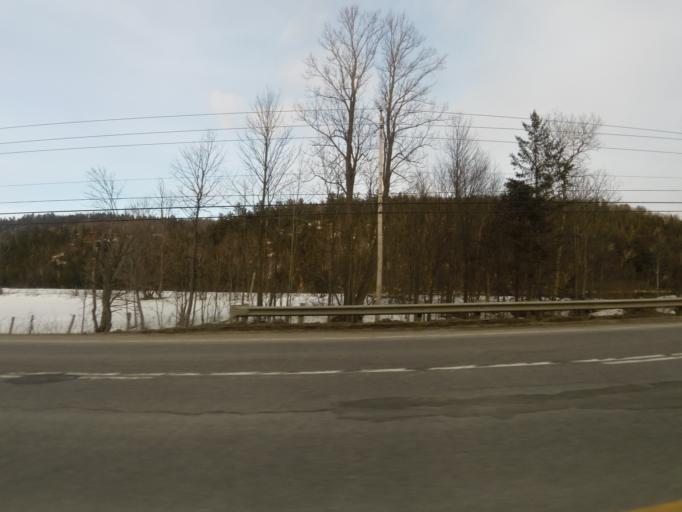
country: CA
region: Quebec
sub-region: Outaouais
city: Wakefield
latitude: 45.7541
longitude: -75.9167
